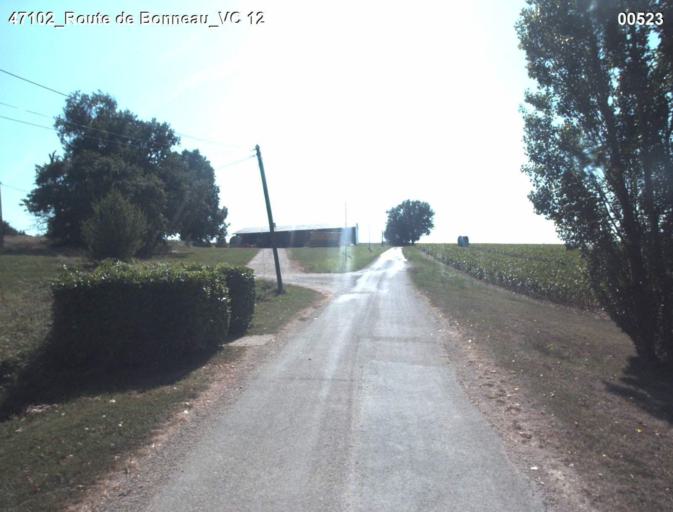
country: FR
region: Aquitaine
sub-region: Departement du Lot-et-Garonne
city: Nerac
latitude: 44.0834
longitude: 0.4111
